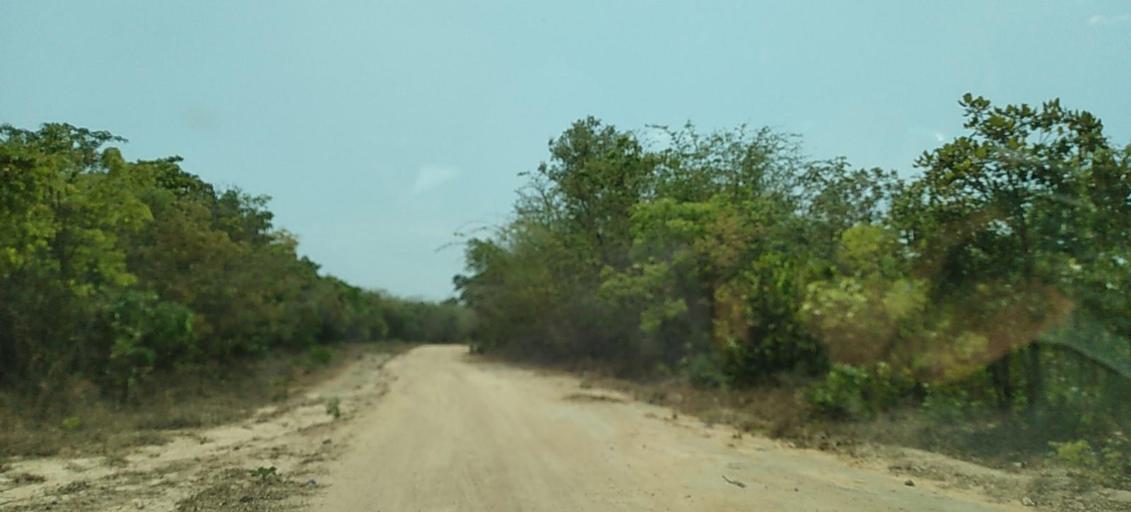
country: ZM
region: Copperbelt
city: Kalulushi
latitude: -12.9414
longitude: 28.1557
